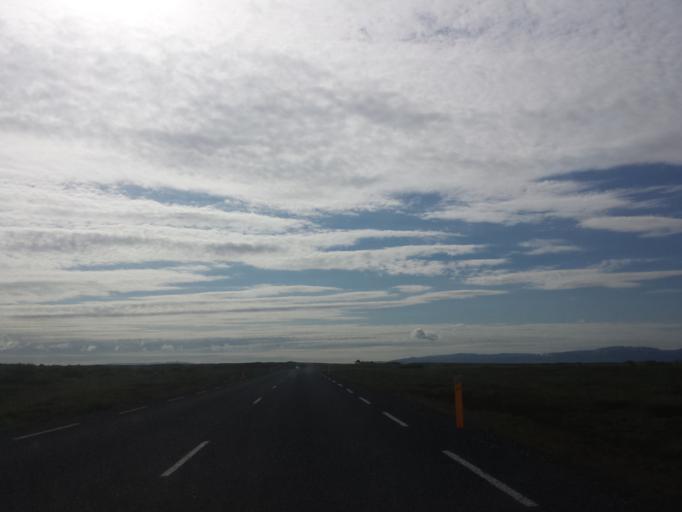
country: IS
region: Northeast
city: Husavik
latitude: 66.0265
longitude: -16.5536
